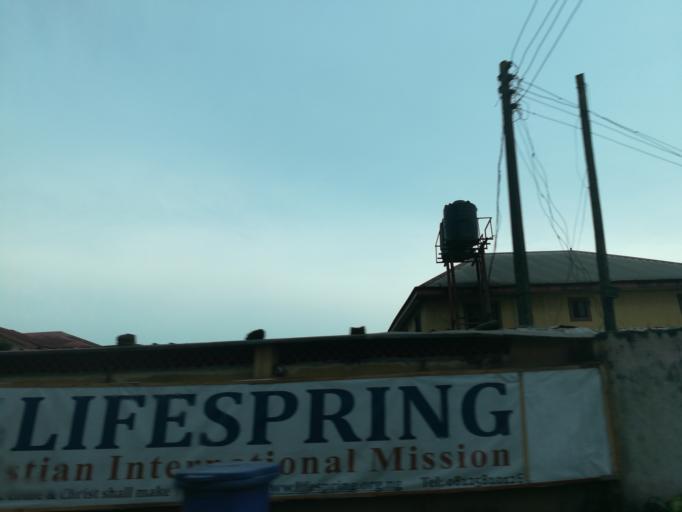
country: NG
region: Rivers
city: Port Harcourt
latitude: 4.8242
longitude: 7.0278
